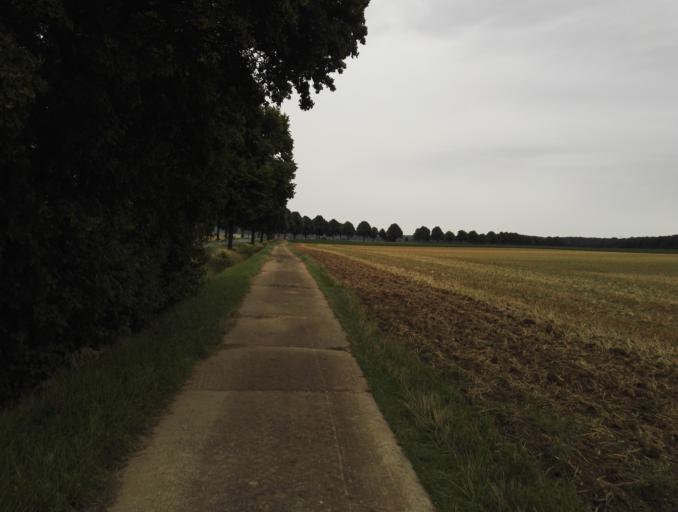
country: DE
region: Lower Saxony
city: Hildesheim
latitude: 52.1388
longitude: 10.0265
